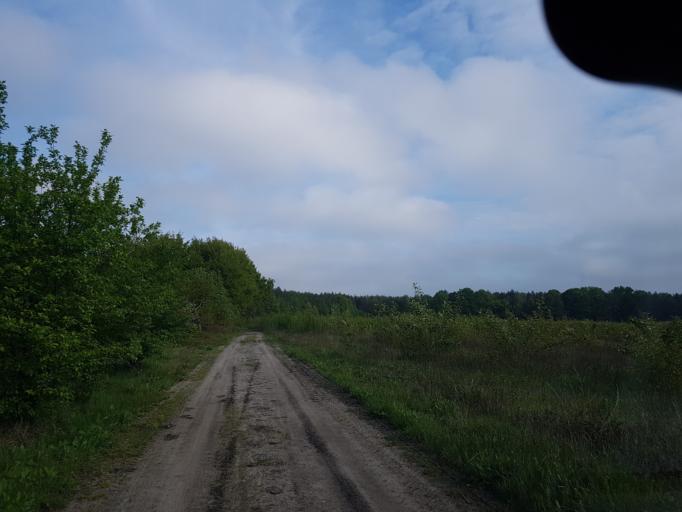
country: DE
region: Brandenburg
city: Finsterwalde
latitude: 51.5764
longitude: 13.6558
